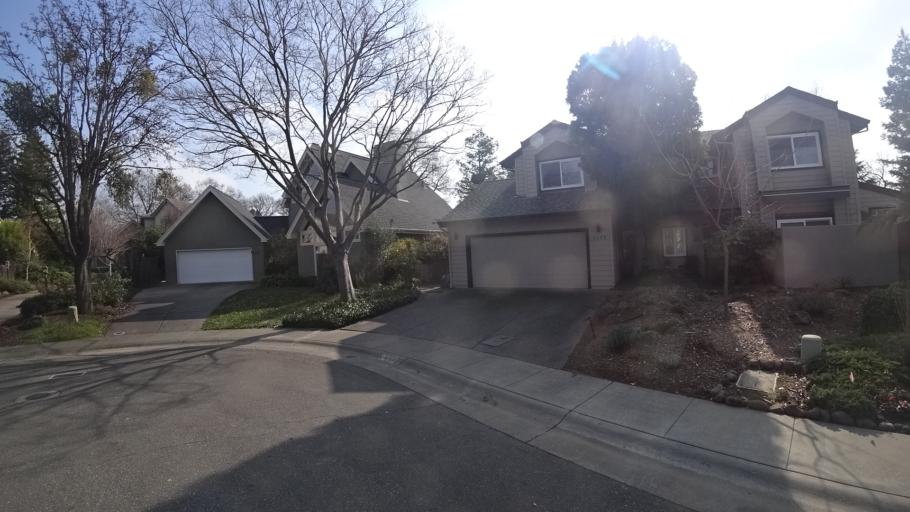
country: US
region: California
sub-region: Yolo County
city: Davis
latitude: 38.5718
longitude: -121.7552
